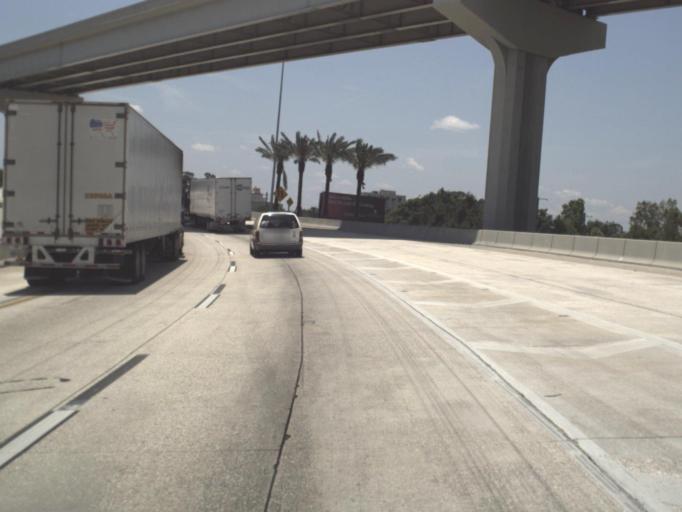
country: US
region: Florida
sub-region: Duval County
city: Jacksonville
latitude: 30.3205
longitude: -81.6818
